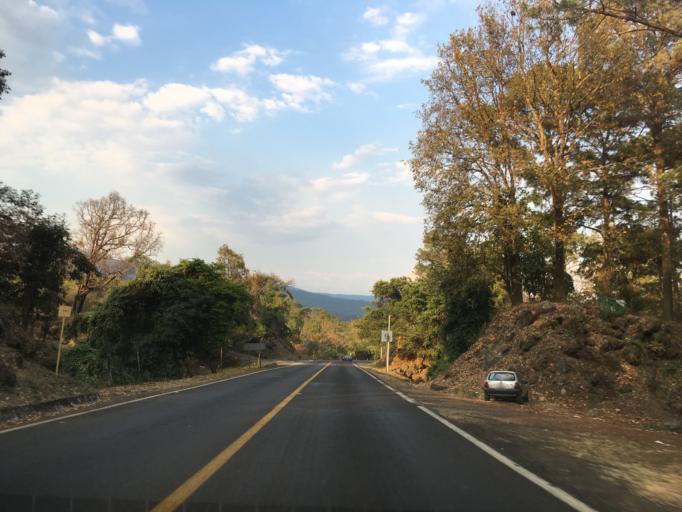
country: MX
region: Michoacan
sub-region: Uruapan
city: Toreo Bajo (El Toreo Bajo)
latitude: 19.4525
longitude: -101.9689
